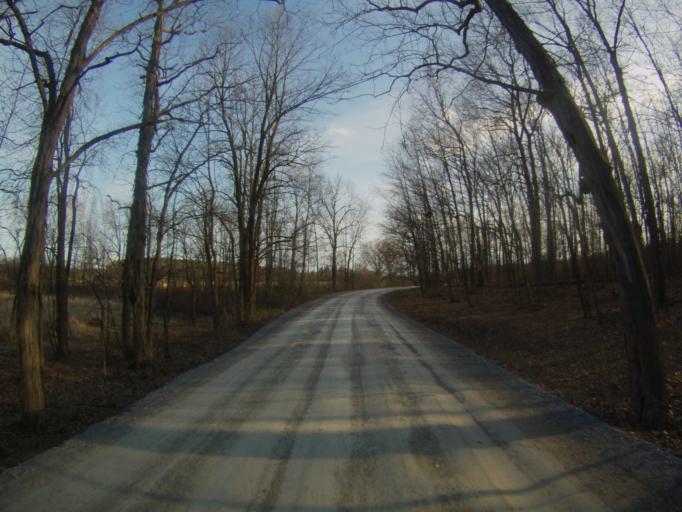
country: US
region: New York
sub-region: Essex County
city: Port Henry
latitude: 44.0764
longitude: -73.3501
